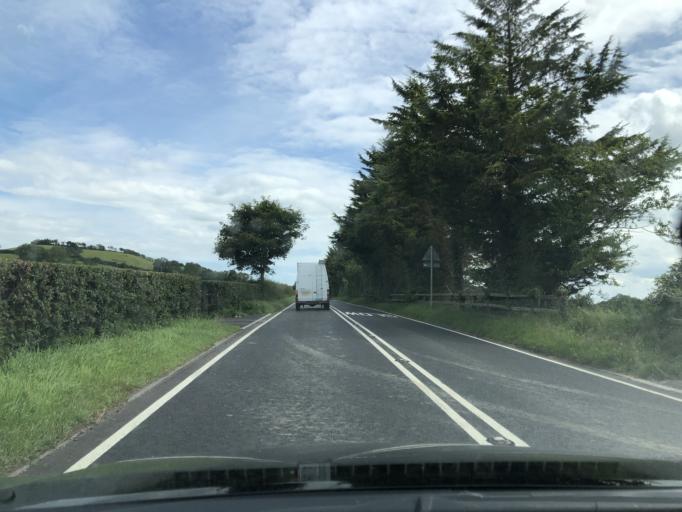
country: GB
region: Northern Ireland
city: Annahilt
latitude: 54.4374
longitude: -5.9373
